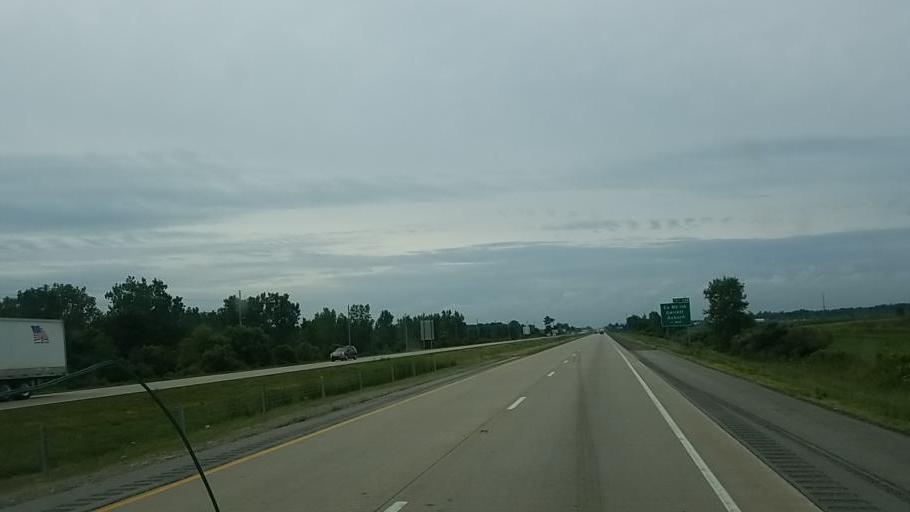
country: US
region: Indiana
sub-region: DeKalb County
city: Auburn
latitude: 41.3486
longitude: -85.0880
